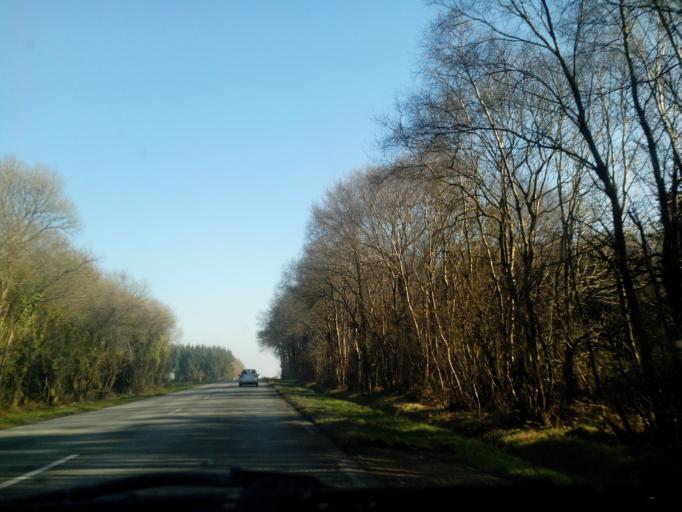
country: FR
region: Brittany
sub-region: Departement des Cotes-d'Armor
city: Merdrignac
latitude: 48.1975
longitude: -2.4715
